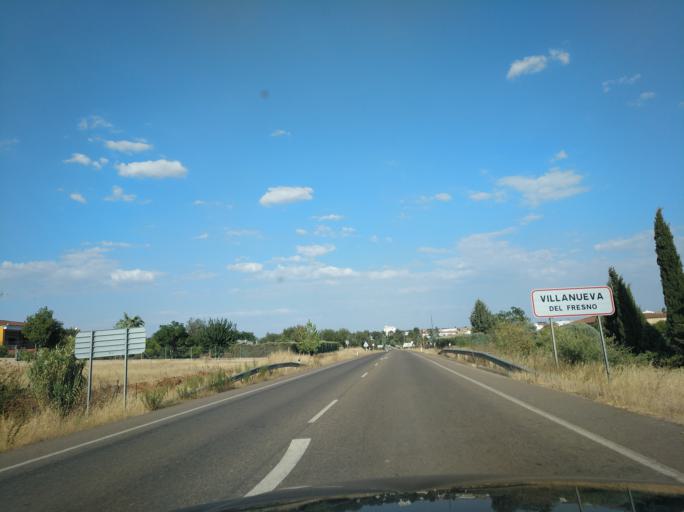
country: ES
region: Extremadura
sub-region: Provincia de Badajoz
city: Villanueva del Fresno
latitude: 38.3775
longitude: -7.1746
